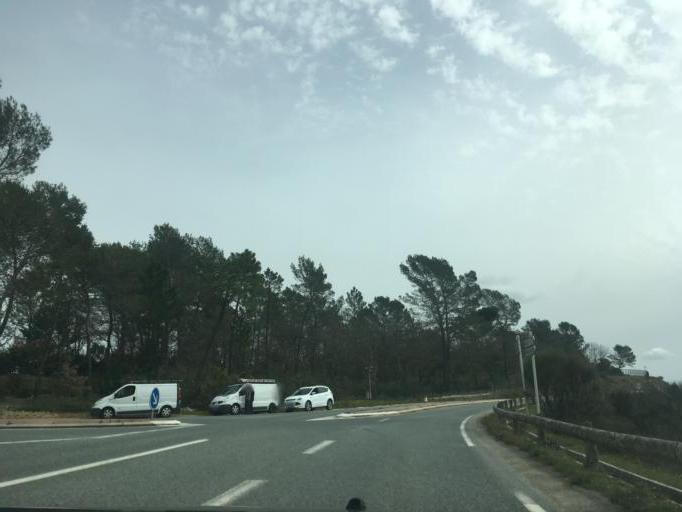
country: FR
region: Provence-Alpes-Cote d'Azur
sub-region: Departement du Var
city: Callian
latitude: 43.5904
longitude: 6.7317
